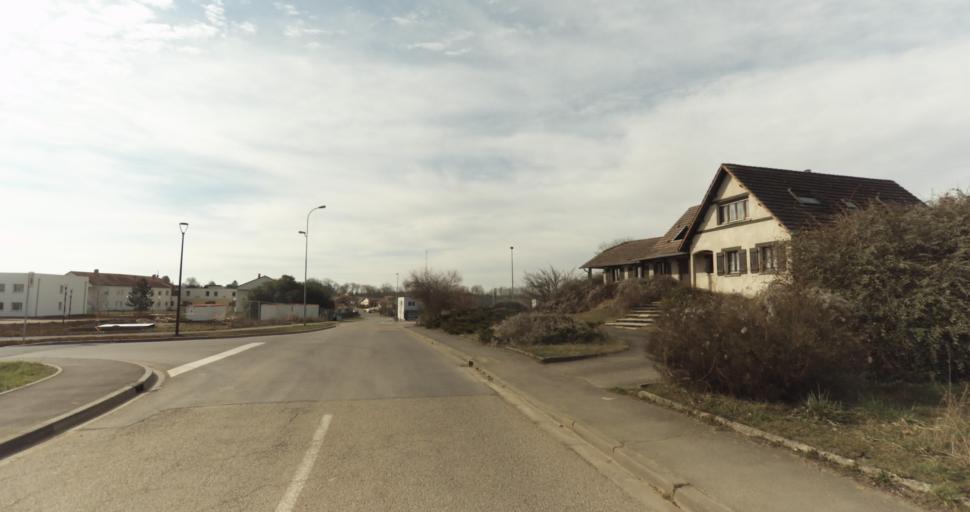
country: FR
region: Lorraine
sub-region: Departement de Meurthe-et-Moselle
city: Jarny
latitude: 49.1606
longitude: 5.8715
